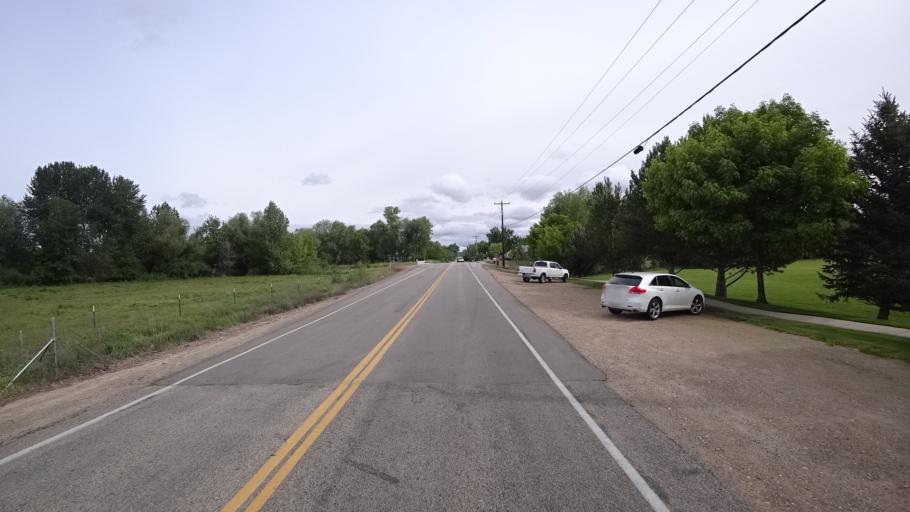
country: US
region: Idaho
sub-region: Ada County
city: Eagle
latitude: 43.7088
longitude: -116.3539
